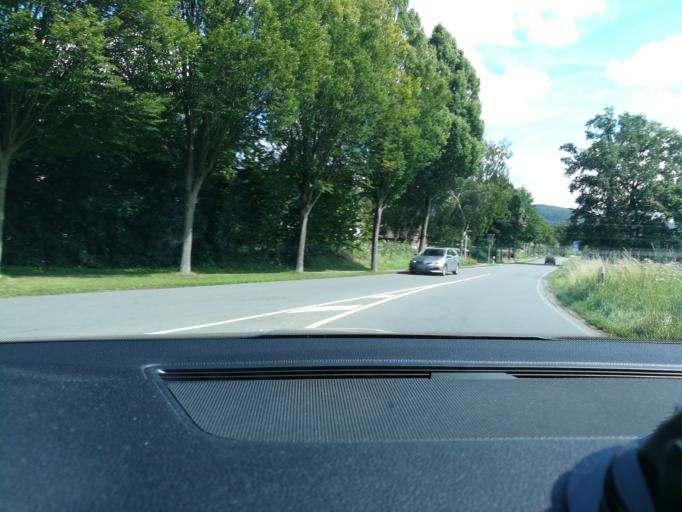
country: DE
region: North Rhine-Westphalia
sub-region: Regierungsbezirk Detmold
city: Huellhorst
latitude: 52.2882
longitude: 8.6658
